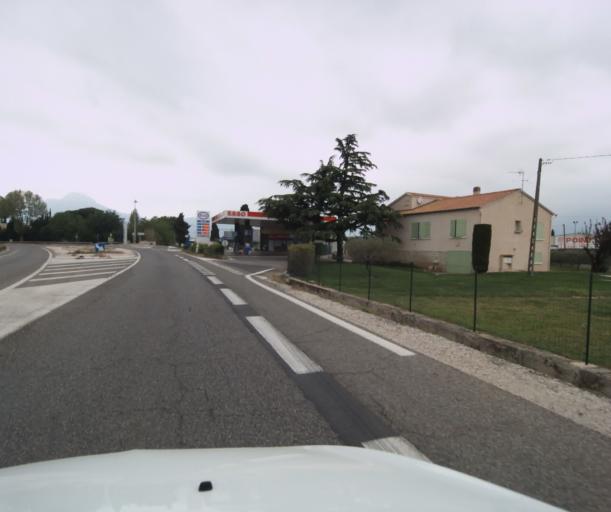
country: FR
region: Provence-Alpes-Cote d'Azur
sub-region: Departement du Var
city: La Crau
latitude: 43.1314
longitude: 6.0707
